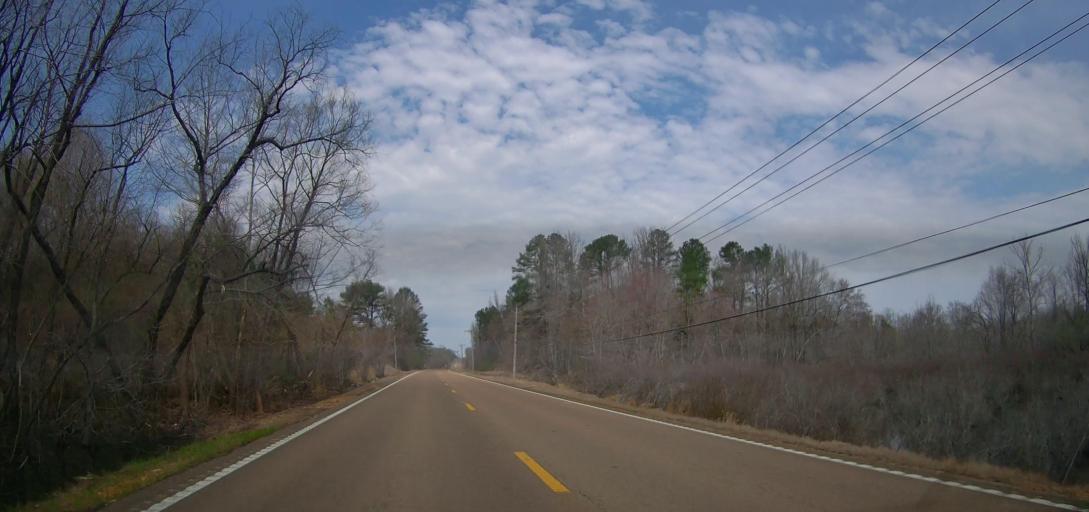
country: US
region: Mississippi
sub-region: Marshall County
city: Holly Springs
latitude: 34.7245
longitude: -89.4165
